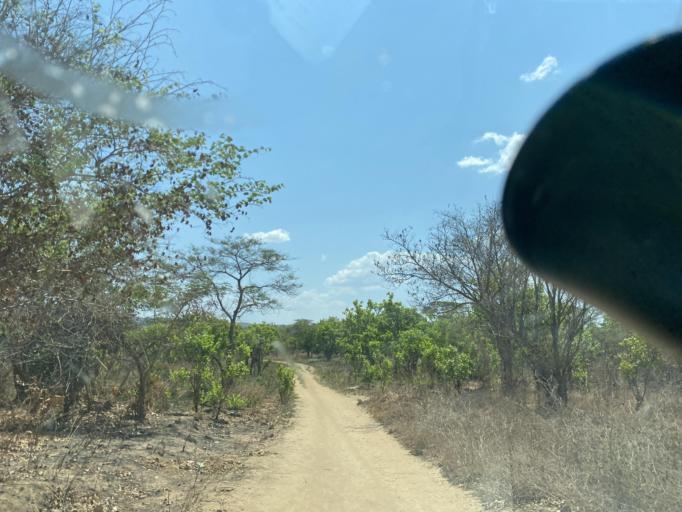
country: ZM
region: Lusaka
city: Chongwe
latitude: -15.0817
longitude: 29.5013
